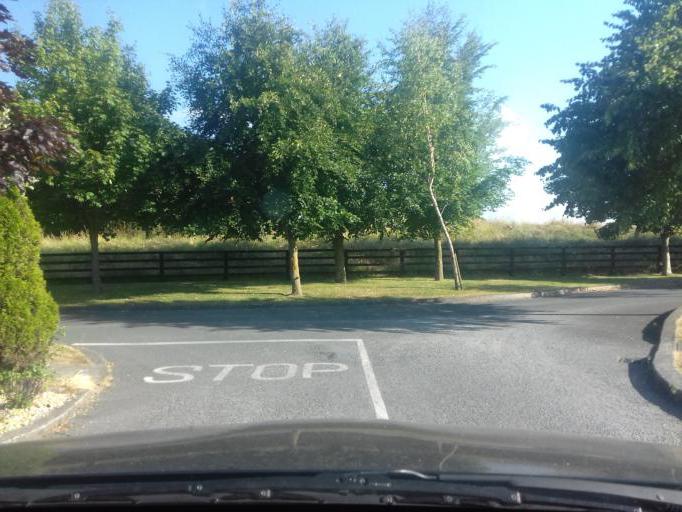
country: IE
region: Leinster
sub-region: Fingal County
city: Blanchardstown
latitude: 53.4339
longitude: -6.3871
